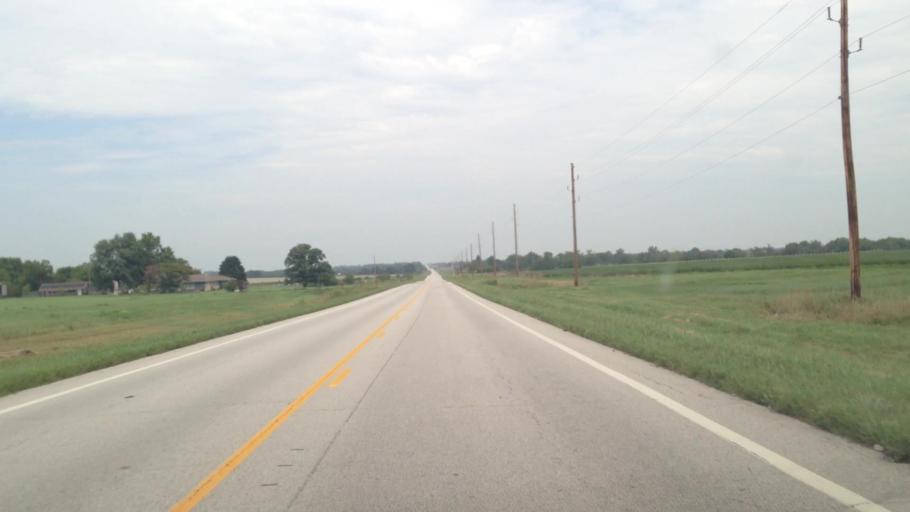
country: US
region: Kansas
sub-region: Allen County
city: Iola
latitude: 37.9372
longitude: -95.1700
